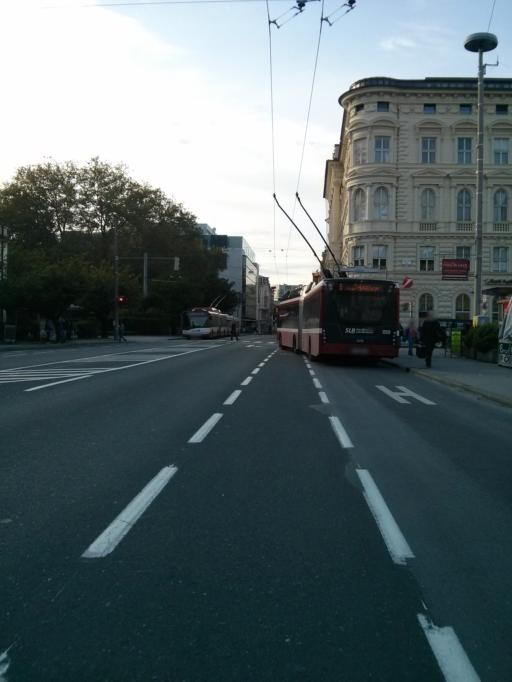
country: AT
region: Salzburg
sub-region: Salzburg Stadt
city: Salzburg
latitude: 47.8058
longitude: 13.0429
